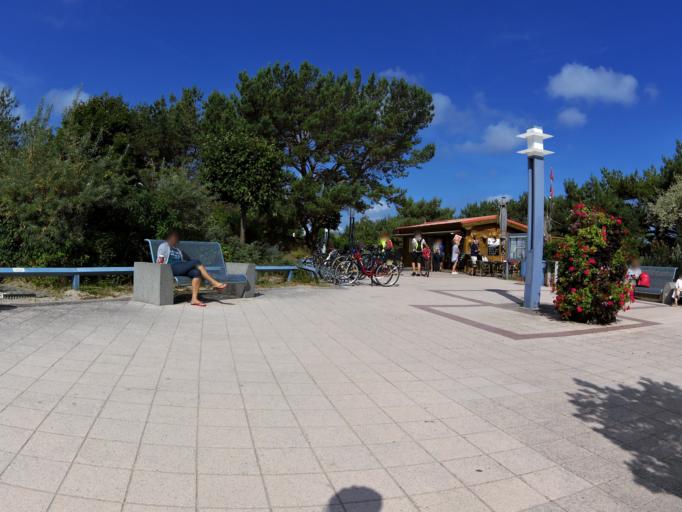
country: DE
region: Mecklenburg-Vorpommern
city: Ostseebad Zinnowitz
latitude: 54.0960
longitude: 13.8796
